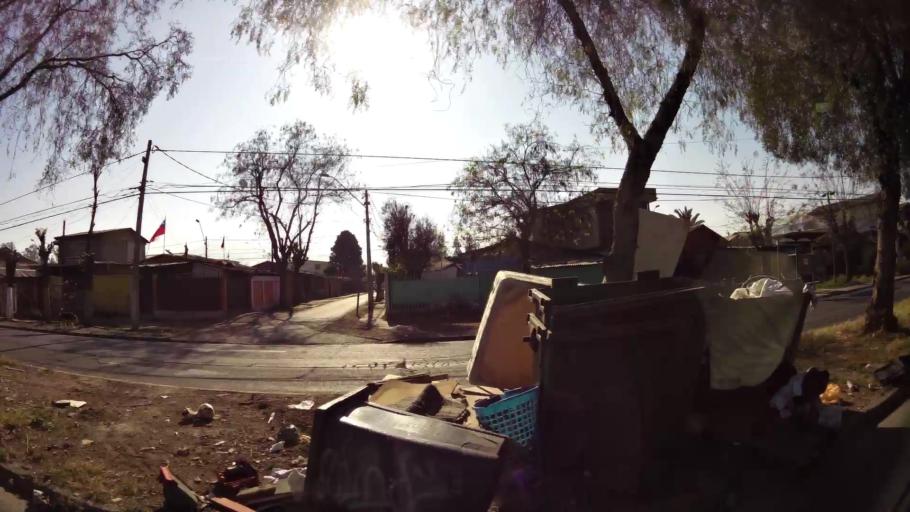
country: CL
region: Santiago Metropolitan
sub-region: Provincia de Santiago
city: Lo Prado
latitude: -33.3812
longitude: -70.6886
